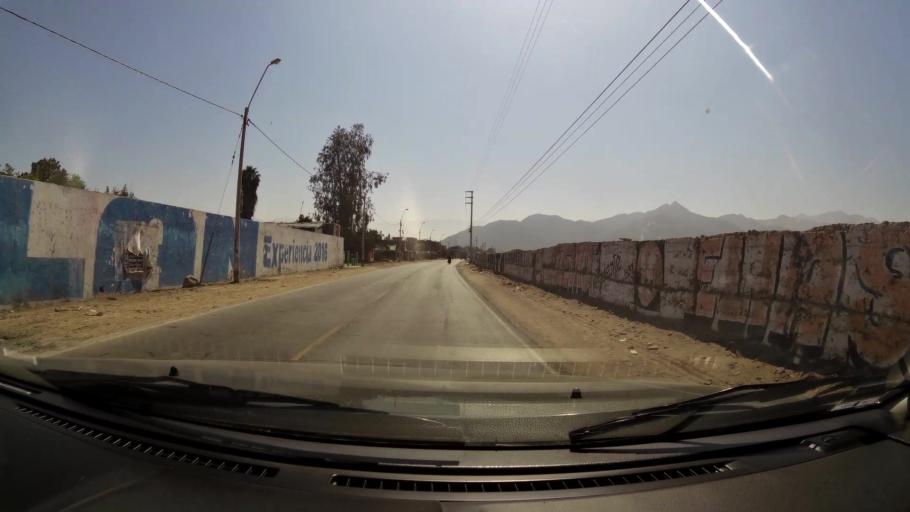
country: PE
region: Ica
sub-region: Provincia de Ica
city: San Juan Bautista
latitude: -13.9990
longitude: -75.7017
